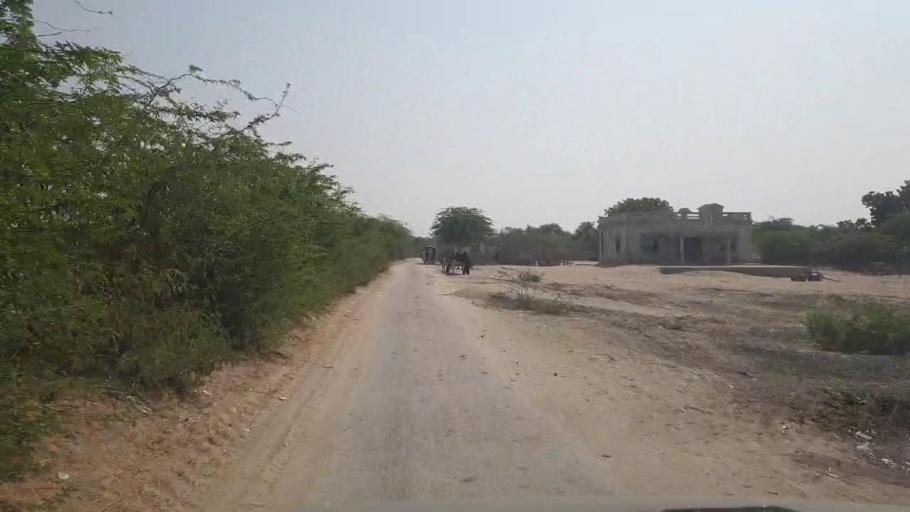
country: PK
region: Sindh
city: Chor
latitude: 25.4795
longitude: 69.7784
